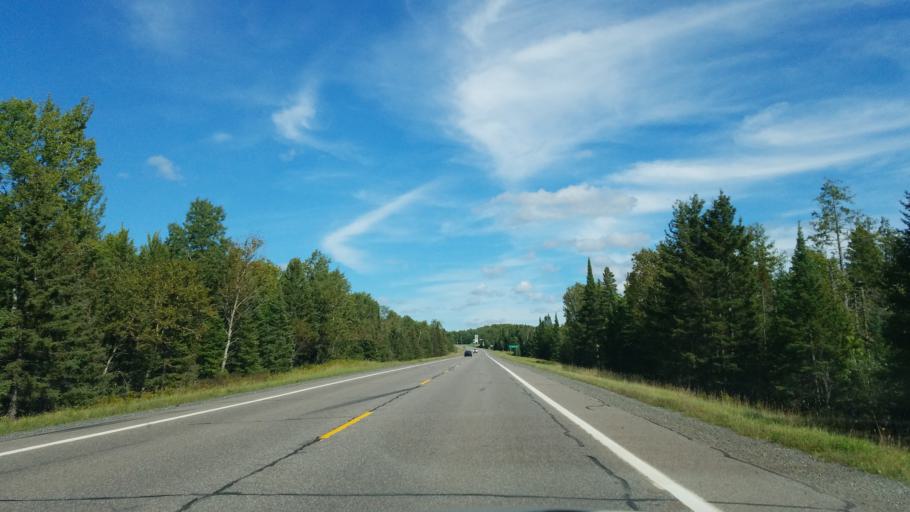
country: US
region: Michigan
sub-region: Baraga County
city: L'Anse
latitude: 46.5455
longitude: -88.5485
